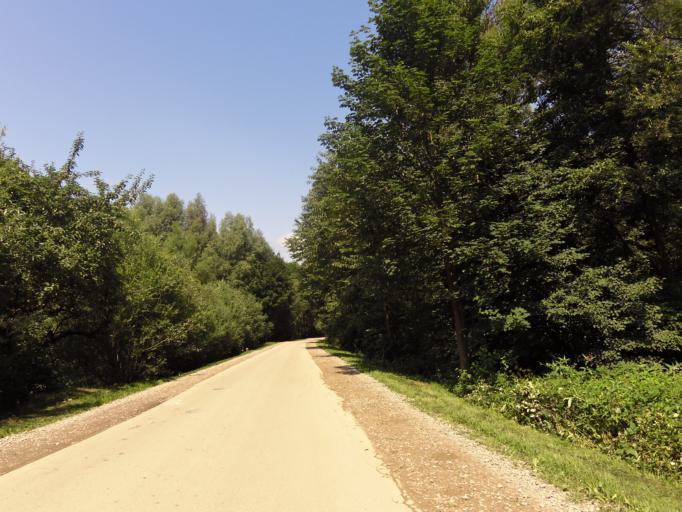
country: PL
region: Silesian Voivodeship
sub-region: Powiat zywiecki
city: Cisiec
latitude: 49.5933
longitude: 19.0982
